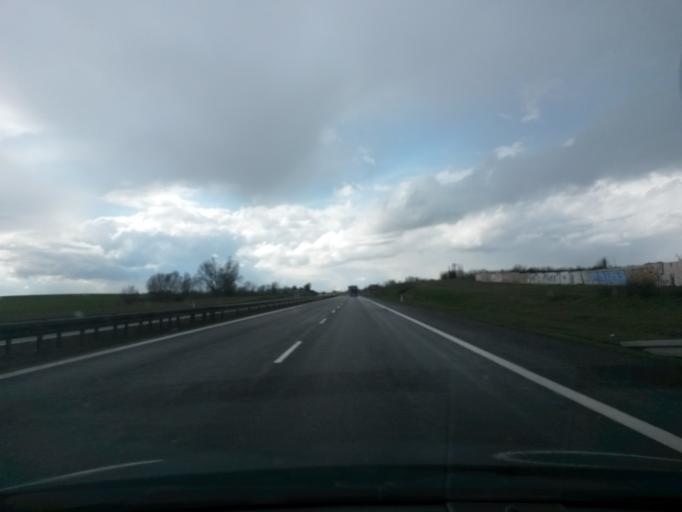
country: PL
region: Greater Poland Voivodeship
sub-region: Powiat poznanski
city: Daszewice
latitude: 52.3419
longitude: 17.0302
